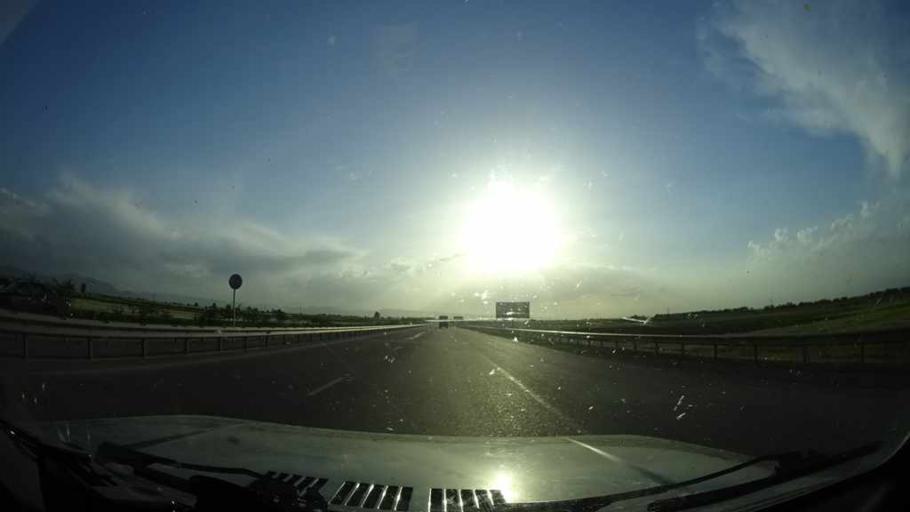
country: AZ
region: Samux
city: Samux
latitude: 40.6897
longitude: 46.5096
